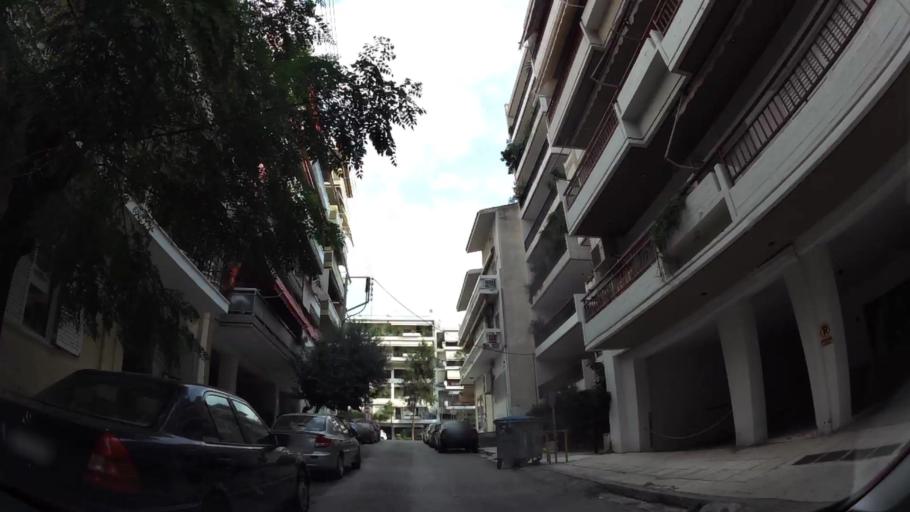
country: GR
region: Attica
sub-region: Nomarchia Athinas
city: Nea Smyrni
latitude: 37.9348
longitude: 23.7148
